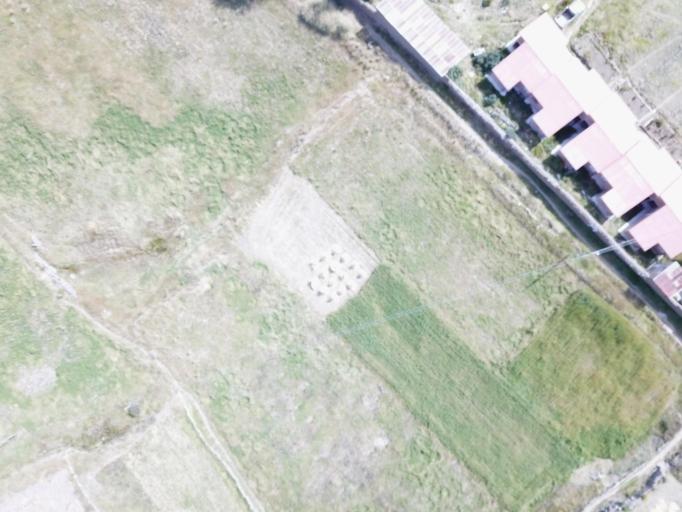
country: BO
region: La Paz
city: Achacachi
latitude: -16.0546
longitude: -68.8117
